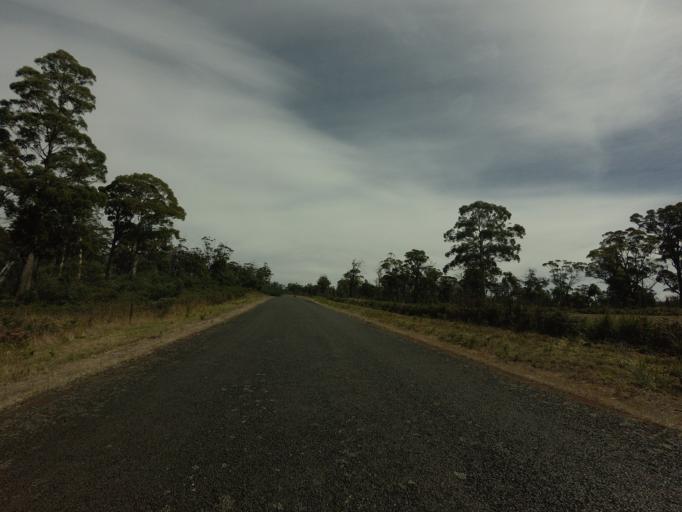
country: AU
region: Tasmania
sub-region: Sorell
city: Sorell
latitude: -42.5552
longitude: 147.6780
